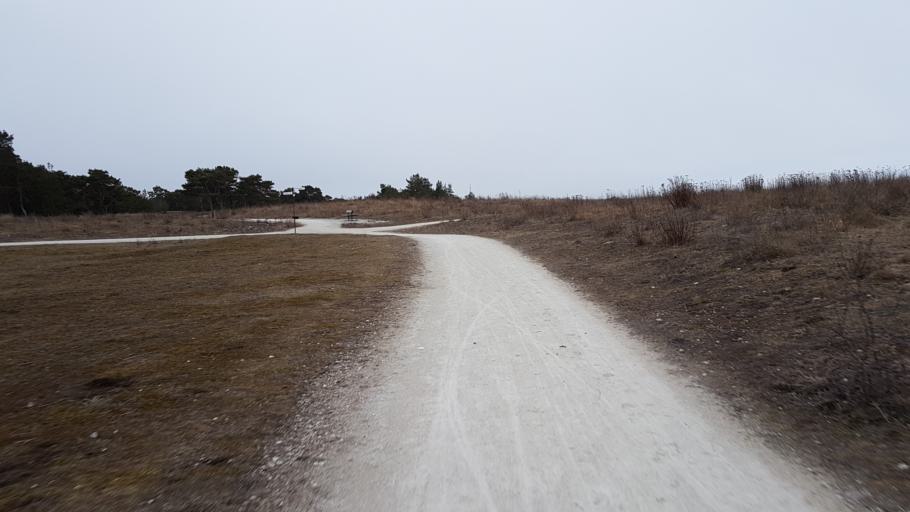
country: SE
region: Gotland
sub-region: Gotland
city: Vibble
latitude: 57.6179
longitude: 18.2630
